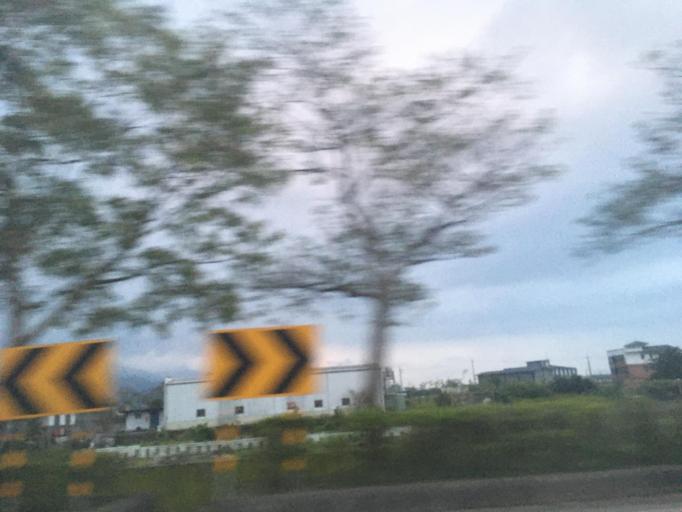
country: TW
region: Taiwan
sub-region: Yilan
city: Yilan
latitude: 24.8036
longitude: 121.7772
